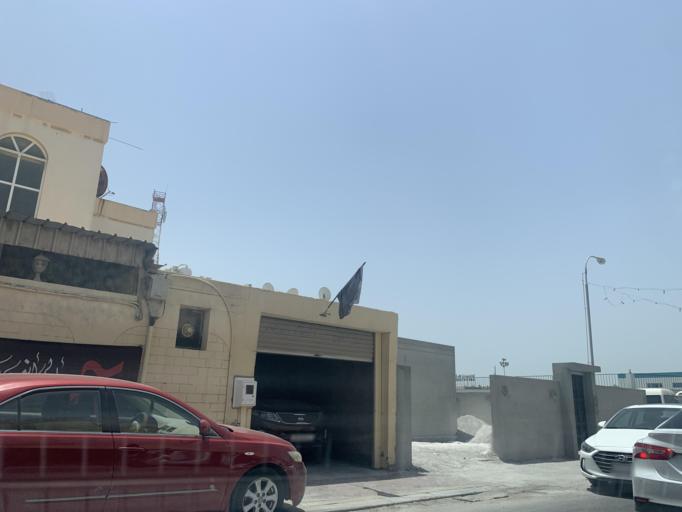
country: BH
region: Central Governorate
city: Madinat Hamad
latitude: 26.1447
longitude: 50.4995
